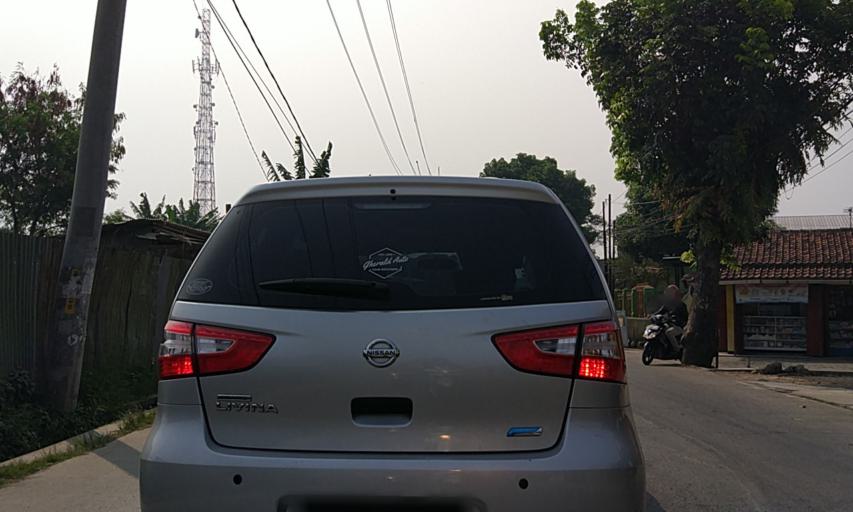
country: ID
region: West Java
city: Soreang
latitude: -7.0197
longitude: 107.5491
